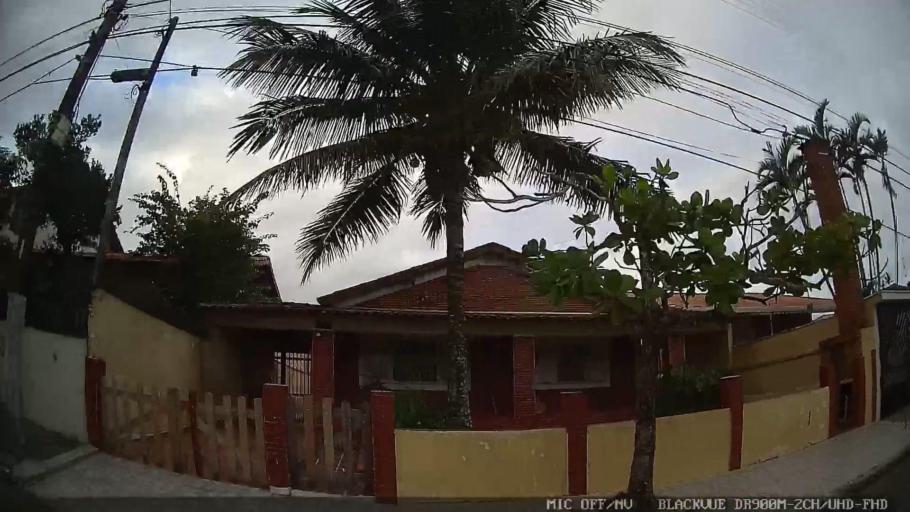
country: BR
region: Sao Paulo
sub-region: Peruibe
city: Peruibe
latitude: -24.3128
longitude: -46.9935
